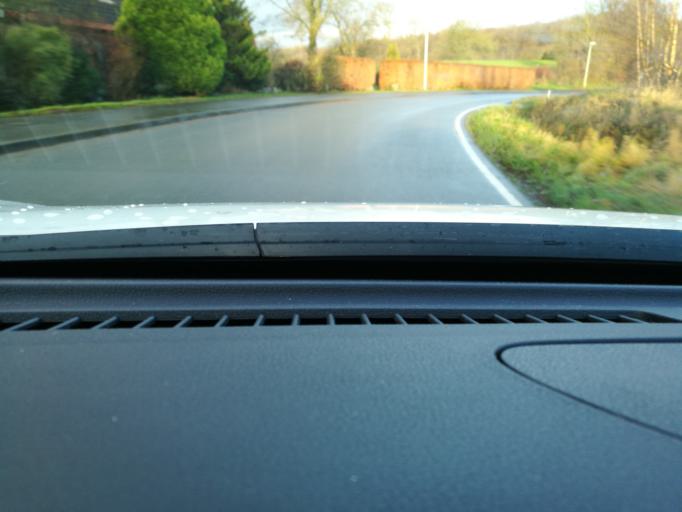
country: DE
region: Schleswig-Holstein
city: Holzbunge
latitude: 54.4036
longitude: 9.6794
